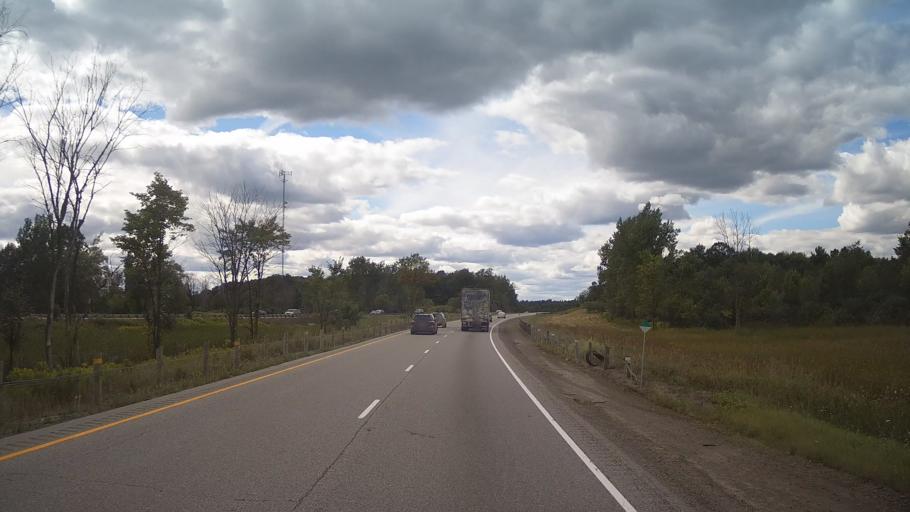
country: CA
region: Ontario
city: Brockville
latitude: 44.5194
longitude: -75.7930
